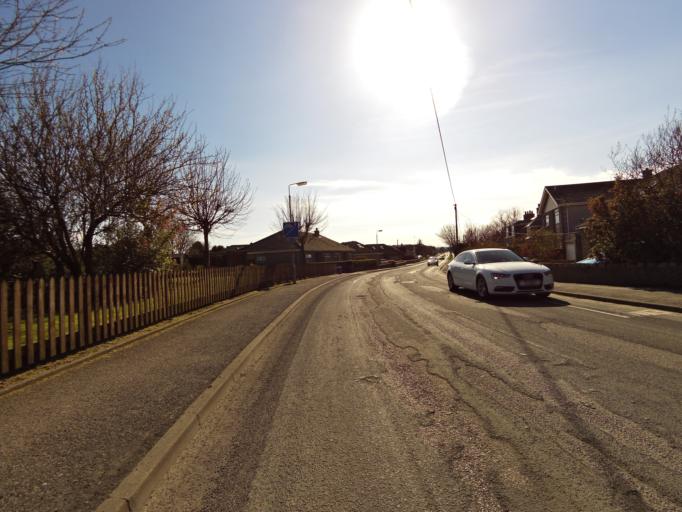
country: GB
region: Scotland
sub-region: Aberdeenshire
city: Portlethen
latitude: 57.0600
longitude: -2.1296
